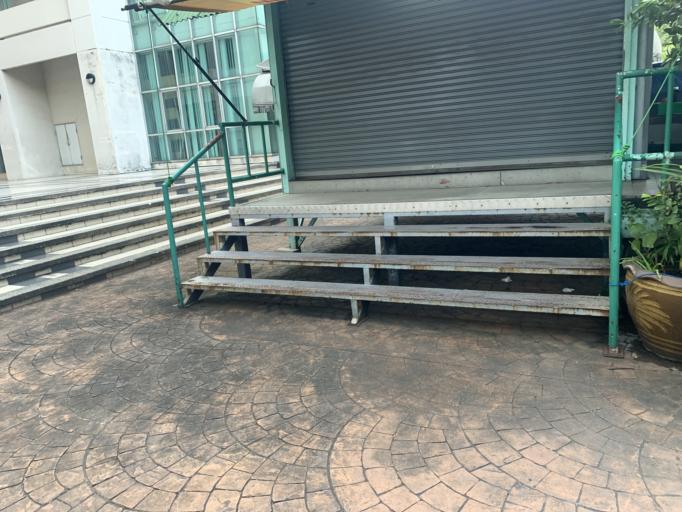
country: TH
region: Bangkok
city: Chatuchak
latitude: 13.8454
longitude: 100.5704
